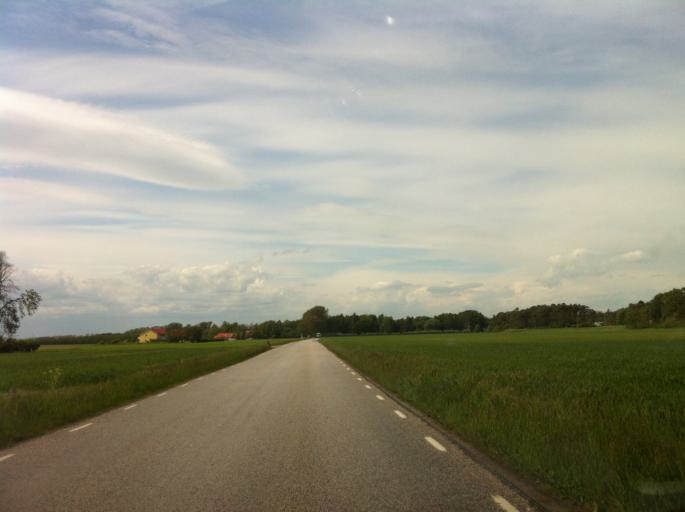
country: SE
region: Skane
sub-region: Kavlinge Kommun
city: Hofterup
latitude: 55.8261
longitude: 12.9290
